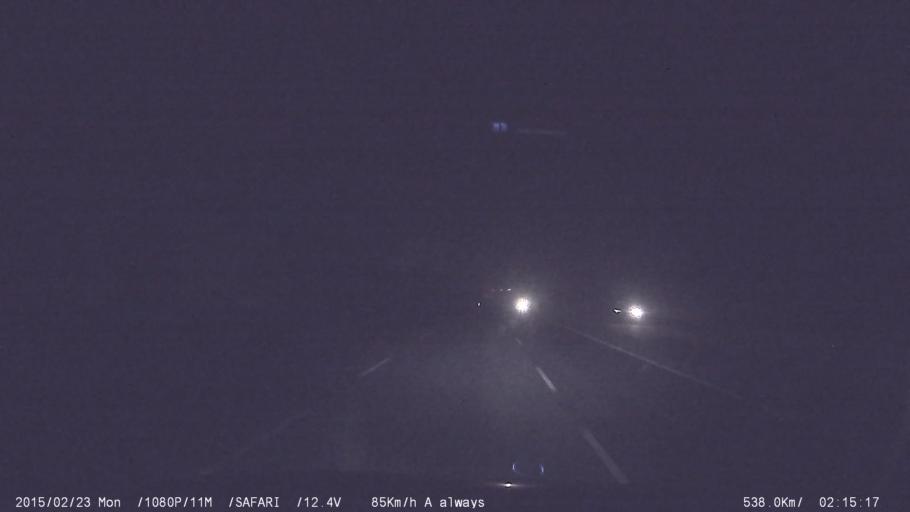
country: IN
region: Tamil Nadu
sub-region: Krishnagiri
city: Hosur
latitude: 12.6890
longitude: 77.9222
